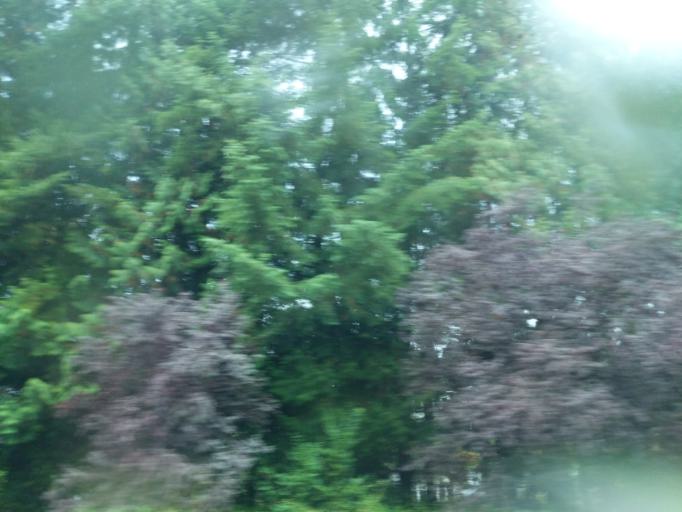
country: US
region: Washington
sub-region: King County
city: Bothell
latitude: 47.7799
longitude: -122.2073
